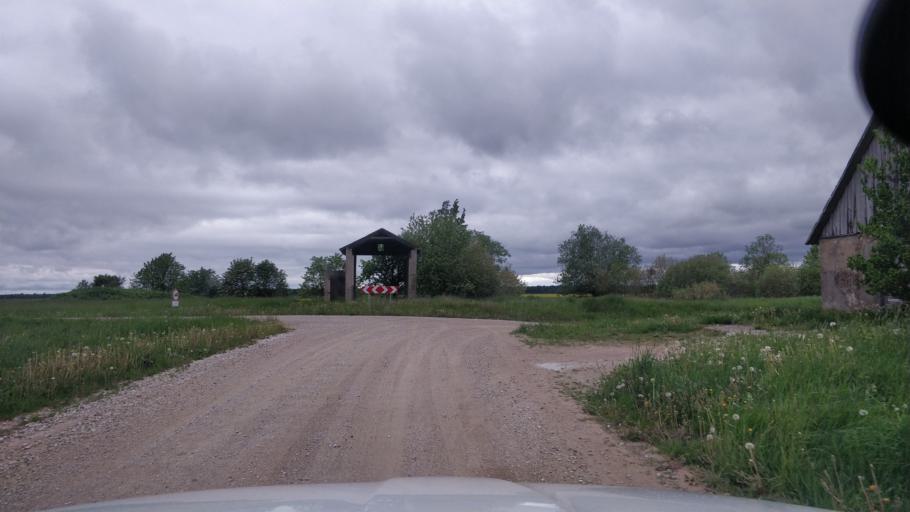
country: EE
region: Raplamaa
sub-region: Maerjamaa vald
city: Marjamaa
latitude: 58.7154
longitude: 24.2321
